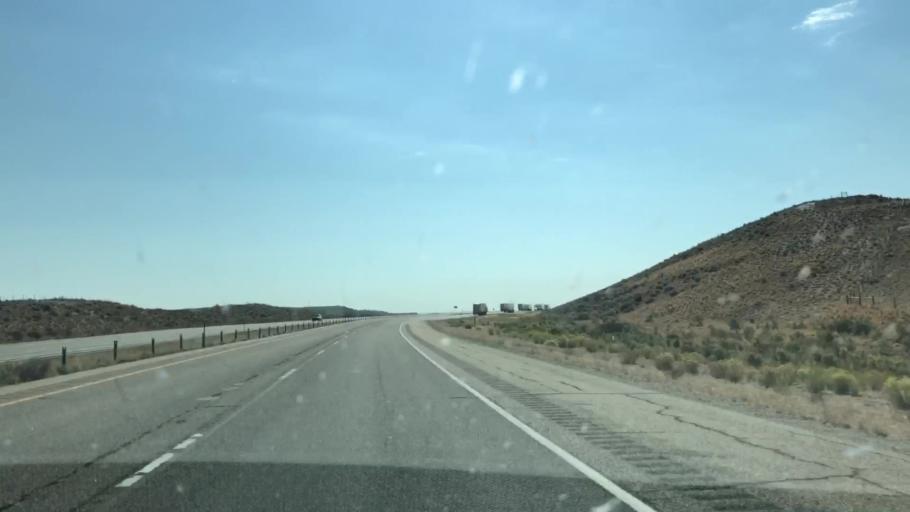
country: US
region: Wyoming
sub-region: Sweetwater County
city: Rock Springs
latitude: 41.6736
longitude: -108.7412
